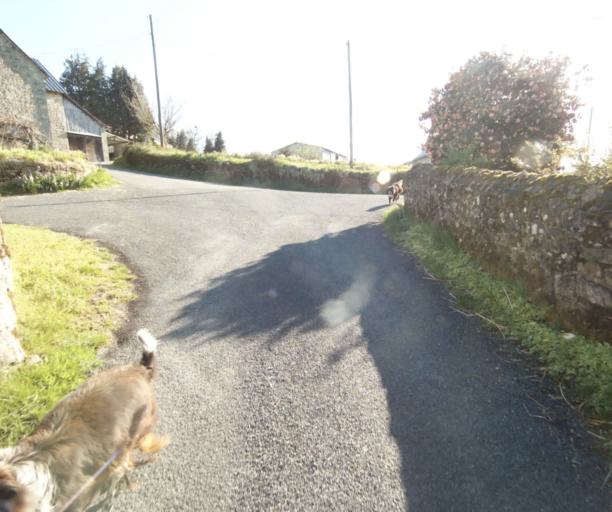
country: FR
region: Limousin
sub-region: Departement de la Correze
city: Correze
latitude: 45.2809
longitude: 1.8828
